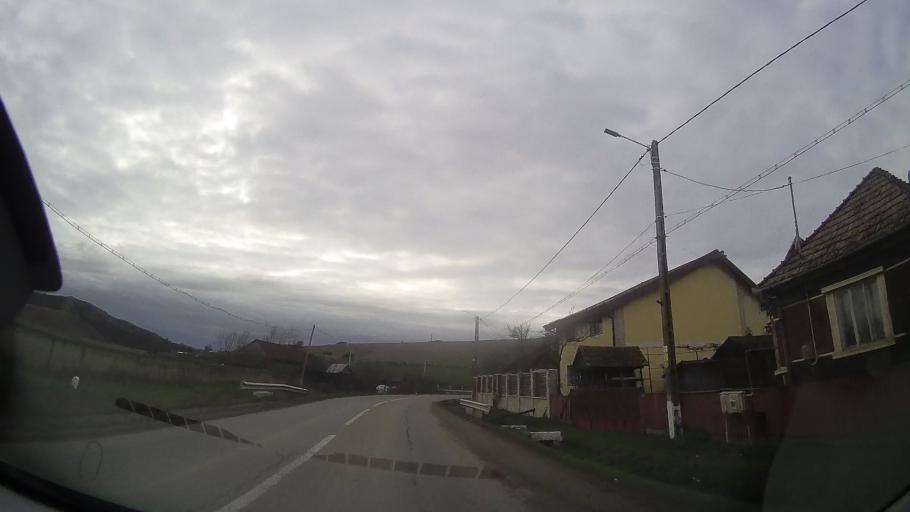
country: RO
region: Bistrita-Nasaud
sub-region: Comuna Budesti
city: Budesti
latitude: 46.8712
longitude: 24.2459
